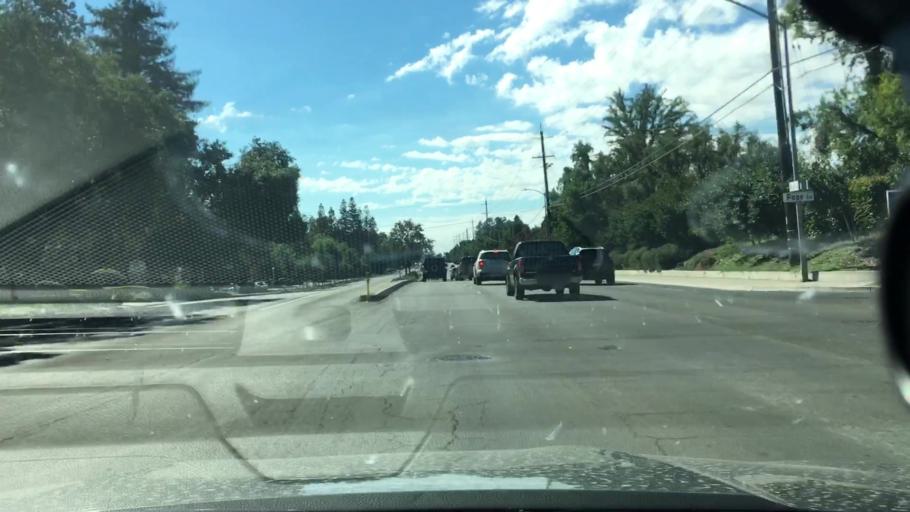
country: US
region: California
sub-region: Sacramento County
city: Arden-Arcade
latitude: 38.6251
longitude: -121.3830
